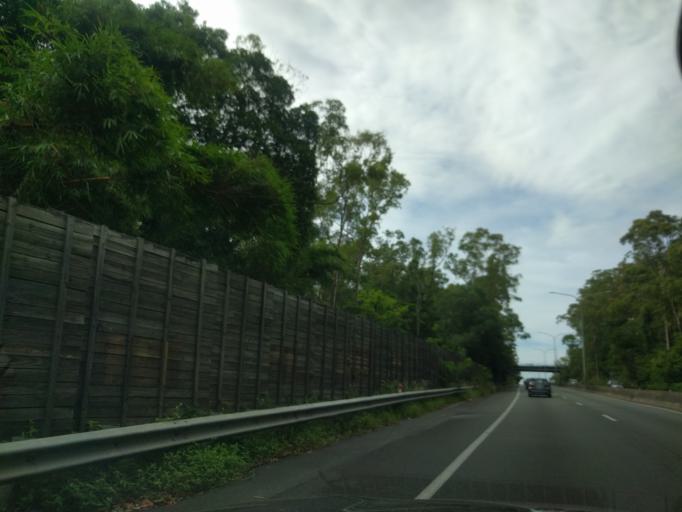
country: AU
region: Queensland
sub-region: Brisbane
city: Kenmore Hills
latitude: -27.5217
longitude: 152.9483
